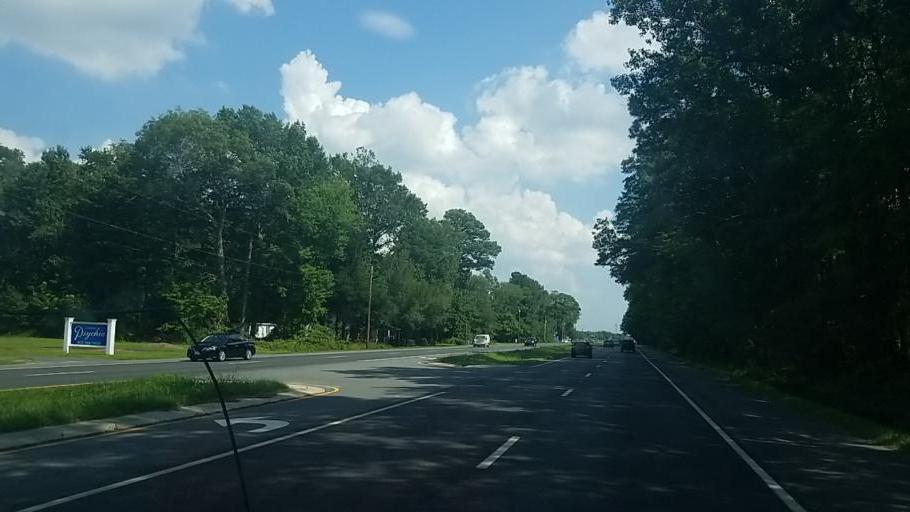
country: US
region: Delaware
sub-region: Sussex County
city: Millsboro
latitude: 38.5520
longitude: -75.2662
